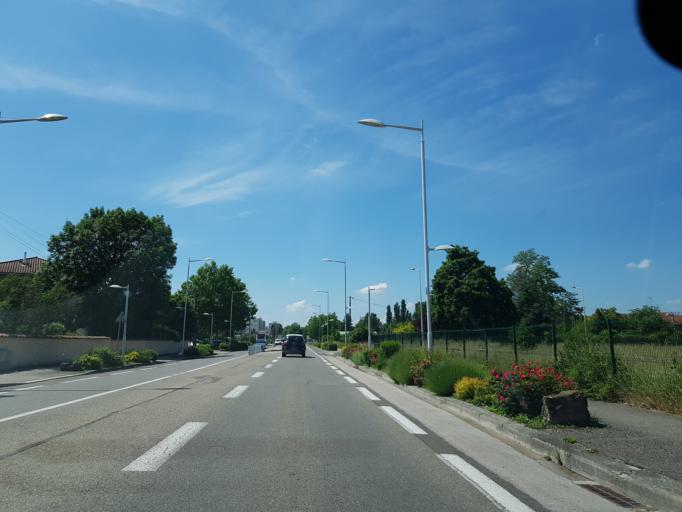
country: FR
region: Rhone-Alpes
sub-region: Departement de l'Ain
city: Bourg-en-Bresse
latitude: 46.2002
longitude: 5.2535
